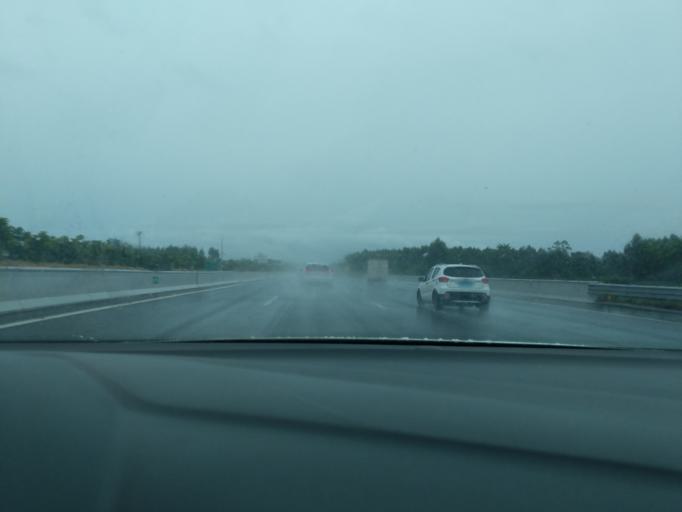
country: CN
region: Guangdong
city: Shuikou
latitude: 22.4841
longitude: 112.7803
